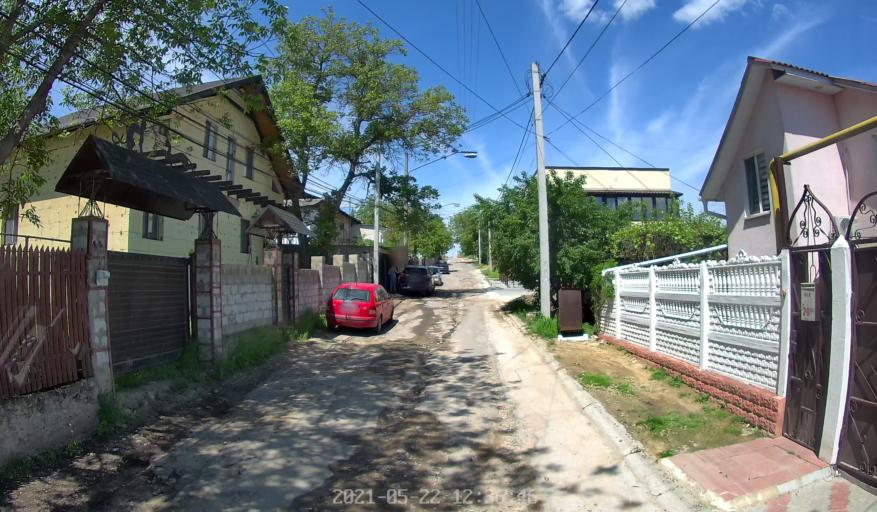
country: MD
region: Chisinau
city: Chisinau
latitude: 47.0509
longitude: 28.8341
